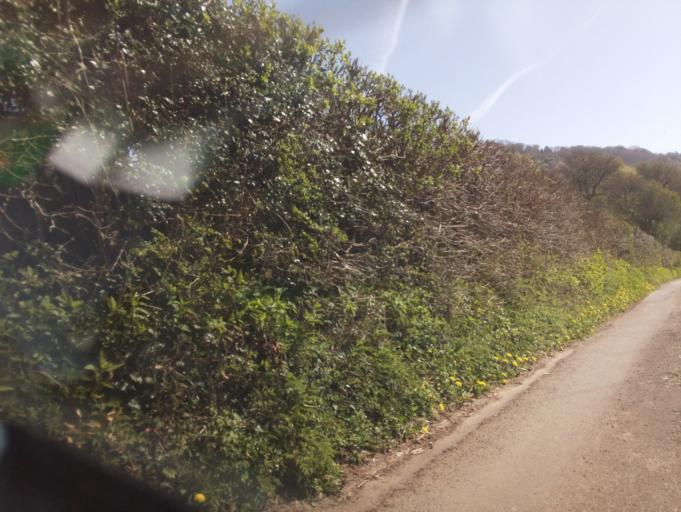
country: GB
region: Wales
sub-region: Monmouthshire
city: Llangwm
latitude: 51.6897
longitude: -2.8219
